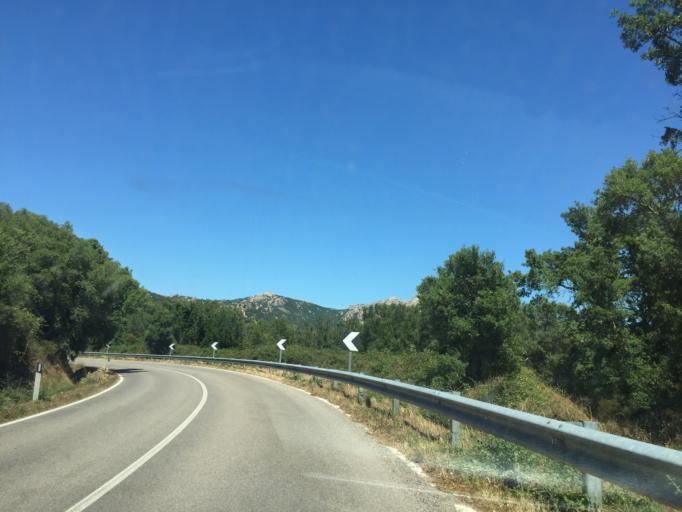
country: IT
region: Sardinia
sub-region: Provincia di Olbia-Tempio
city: Aggius
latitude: 40.9745
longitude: 9.0941
